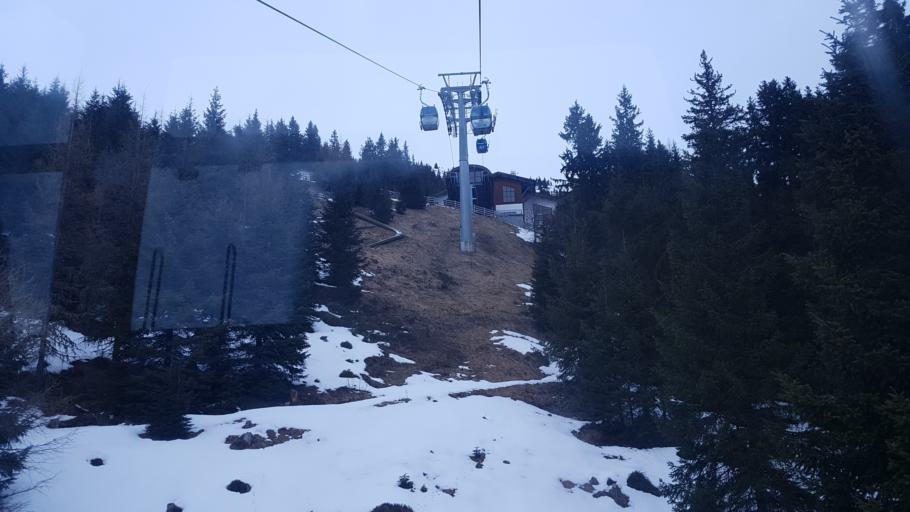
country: AT
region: Salzburg
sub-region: Politischer Bezirk Zell am See
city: Neukirchen am Grossvenediger
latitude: 47.2694
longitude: 12.2809
